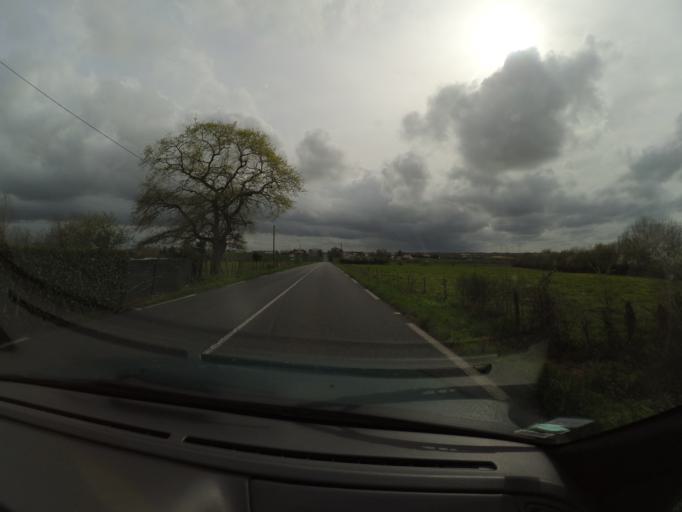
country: FR
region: Pays de la Loire
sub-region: Departement de la Loire-Atlantique
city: La Remaudiere
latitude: 47.2452
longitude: -1.2108
